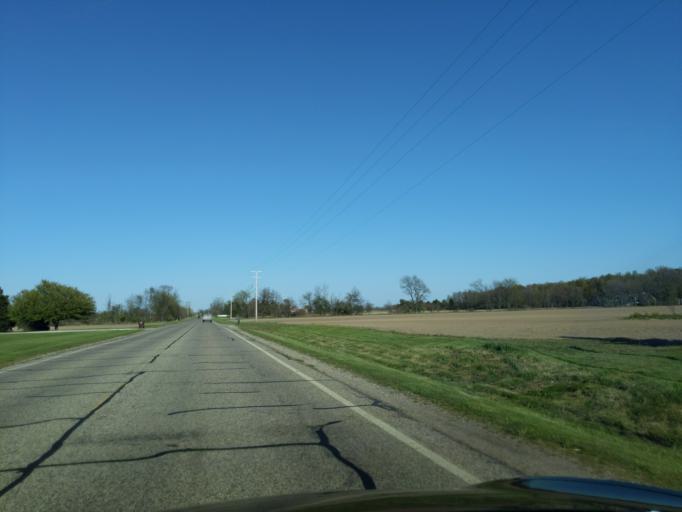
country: US
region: Michigan
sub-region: Ionia County
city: Portland
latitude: 42.8858
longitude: -85.0079
